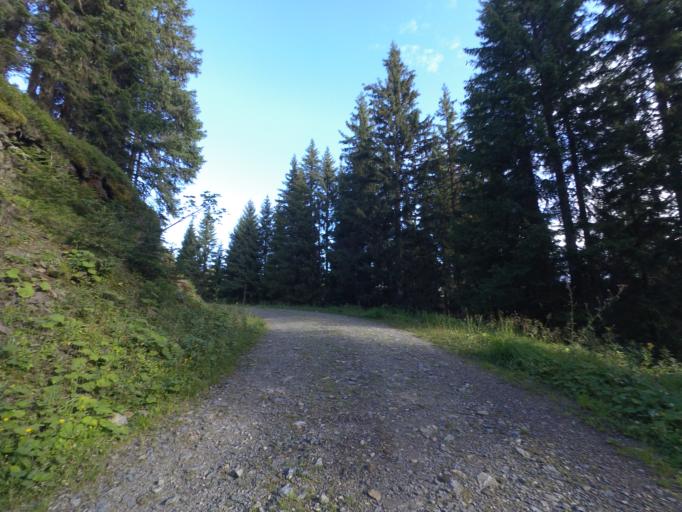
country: AT
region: Salzburg
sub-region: Politischer Bezirk Sankt Johann im Pongau
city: Goldegg
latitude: 47.3522
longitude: 13.0899
